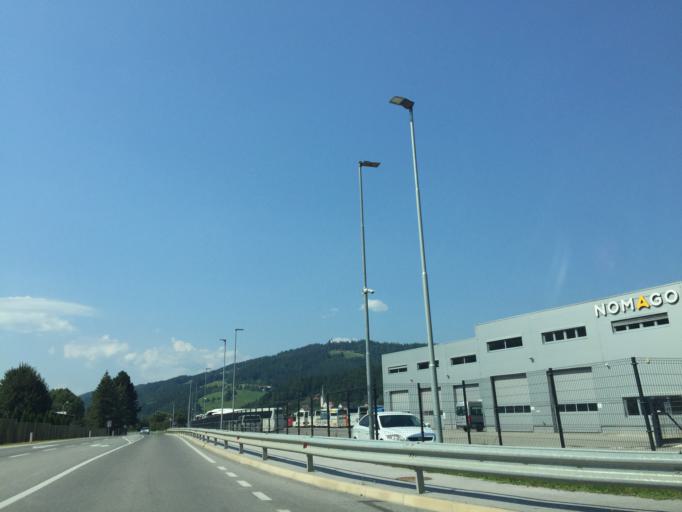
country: SI
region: Slovenj Gradec
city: Pamece
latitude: 46.5265
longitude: 15.0799
